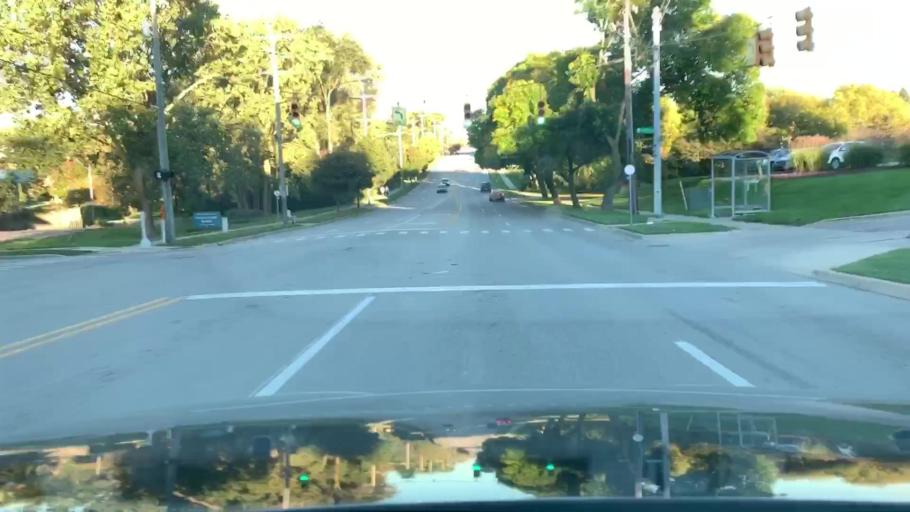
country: US
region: Michigan
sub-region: Kent County
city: East Grand Rapids
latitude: 42.9843
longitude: -85.6206
